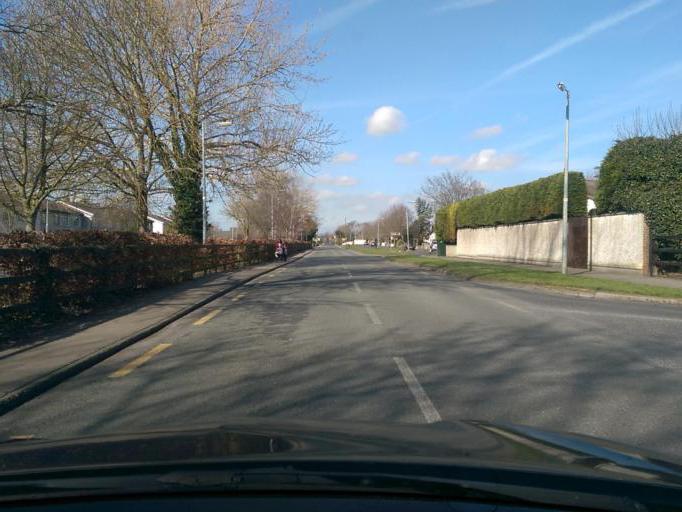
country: IE
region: Leinster
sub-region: Kildare
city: Maynooth
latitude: 53.3727
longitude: -6.5847
